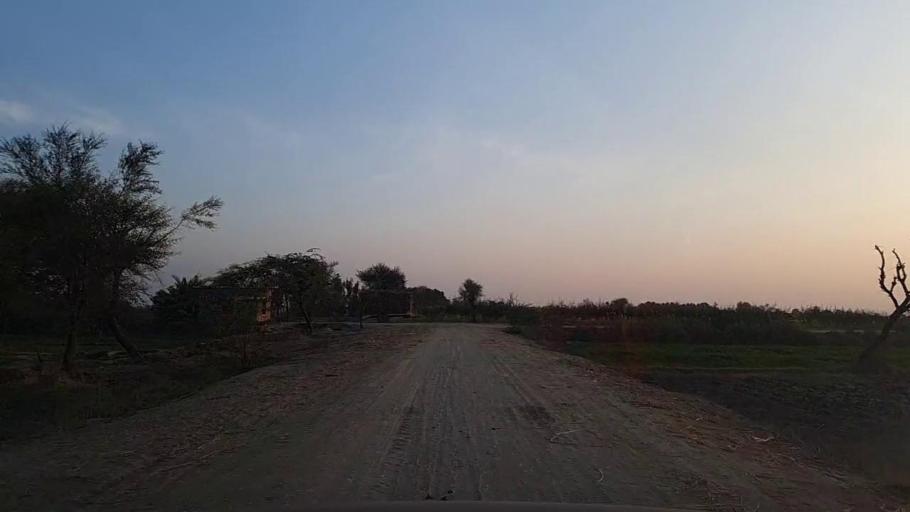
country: PK
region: Sindh
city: Tando Mittha Khan
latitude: 25.9593
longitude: 69.1104
